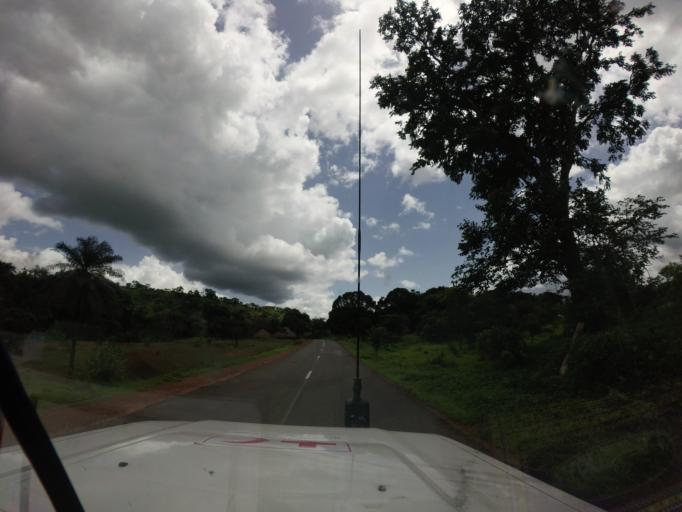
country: SL
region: Northern Province
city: Bindi
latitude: 10.1493
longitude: -11.5603
